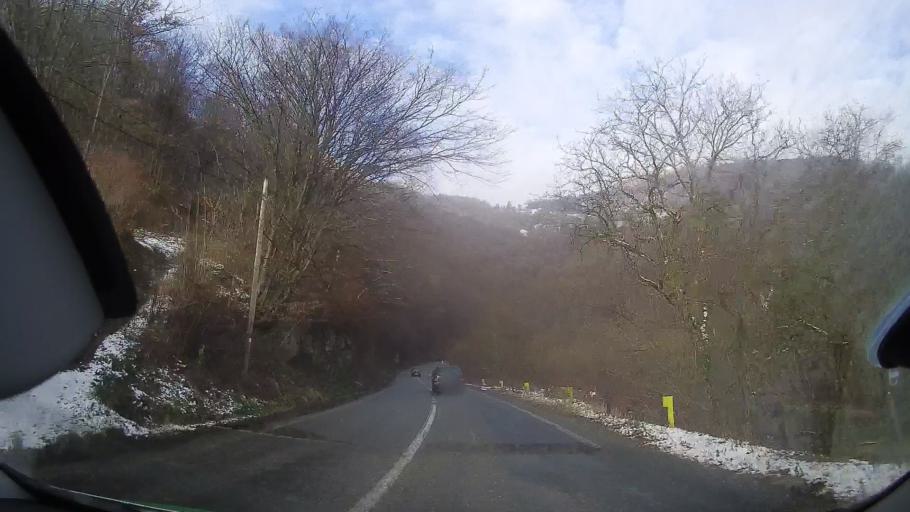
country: RO
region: Alba
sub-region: Oras Baia de Aries
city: Baia de Aries
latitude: 46.3789
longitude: 23.2605
